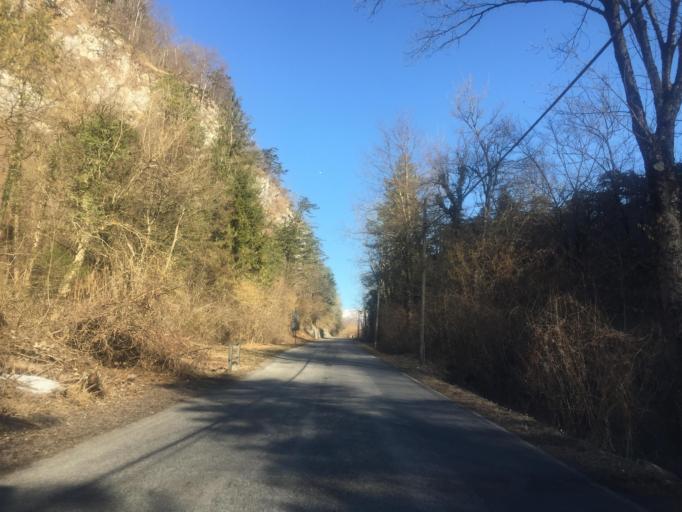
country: IT
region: Friuli Venezia Giulia
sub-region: Provincia di Udine
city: Tolmezzo
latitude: 46.4169
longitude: 13.0507
